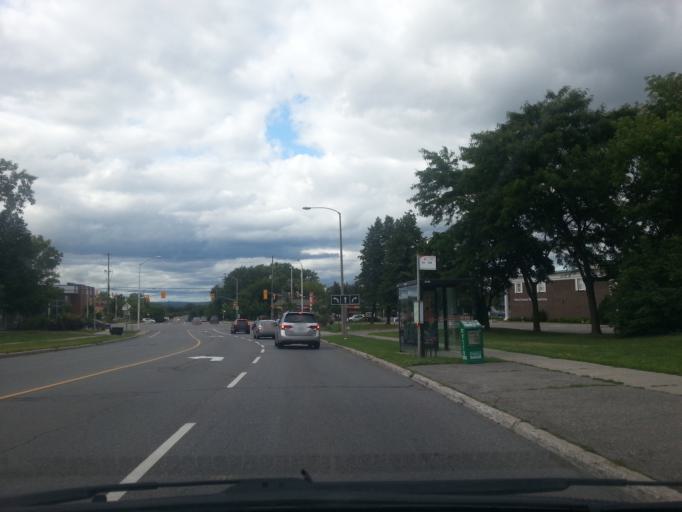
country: CA
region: Quebec
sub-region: Outaouais
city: Gatineau
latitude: 45.4678
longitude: -75.5295
